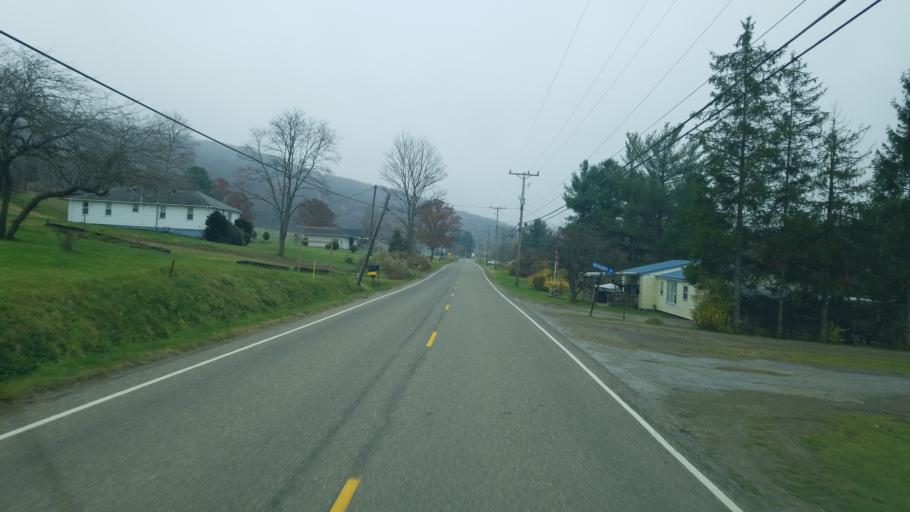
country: US
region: Pennsylvania
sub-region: McKean County
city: Smethport
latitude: 41.8754
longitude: -78.4842
